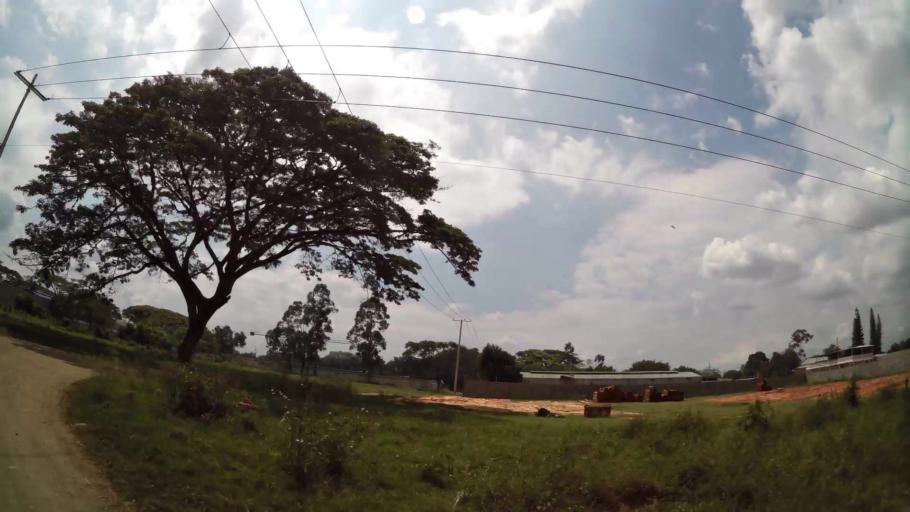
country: CO
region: Valle del Cauca
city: Cali
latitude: 3.5018
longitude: -76.4768
